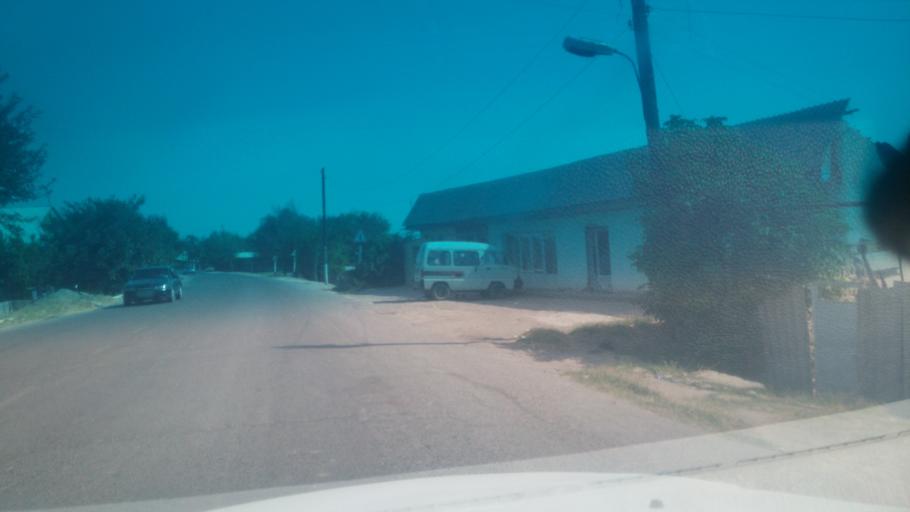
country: UZ
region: Sirdaryo
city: Sirdaryo
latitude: 40.8193
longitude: 68.6701
